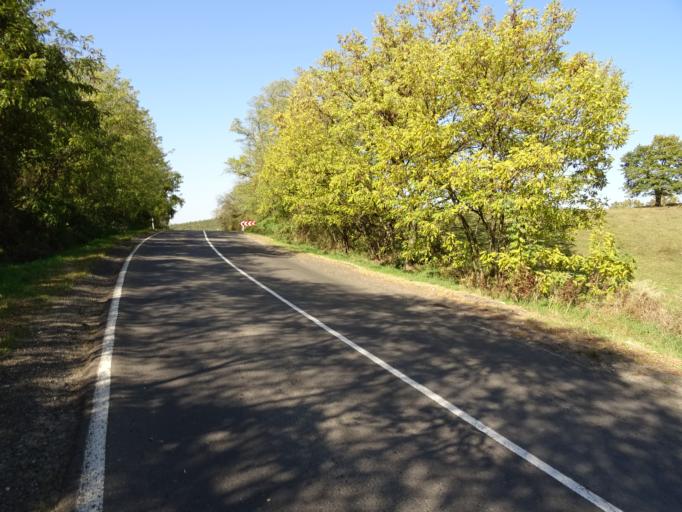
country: HU
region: Nograd
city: Salgotarjan
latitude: 48.0720
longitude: 19.7493
